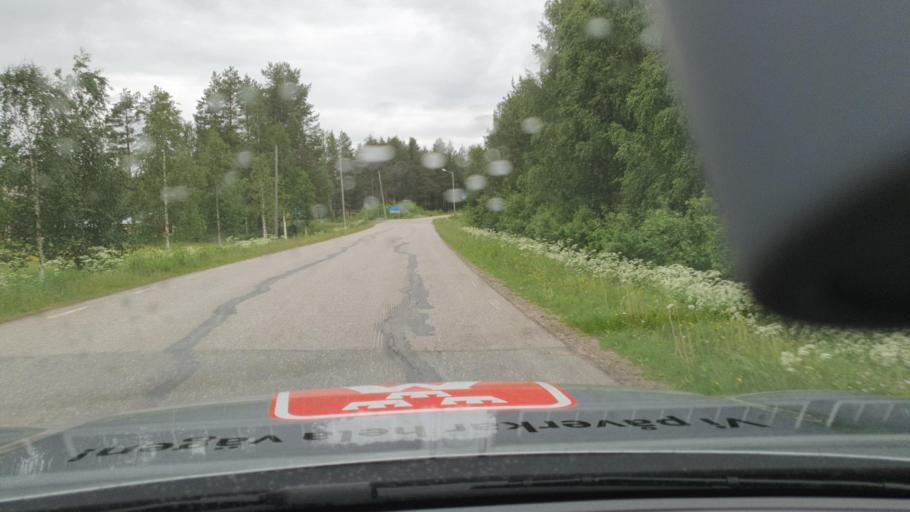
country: SE
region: Norrbotten
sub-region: Overkalix Kommun
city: OEverkalix
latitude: 66.3522
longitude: 22.7989
